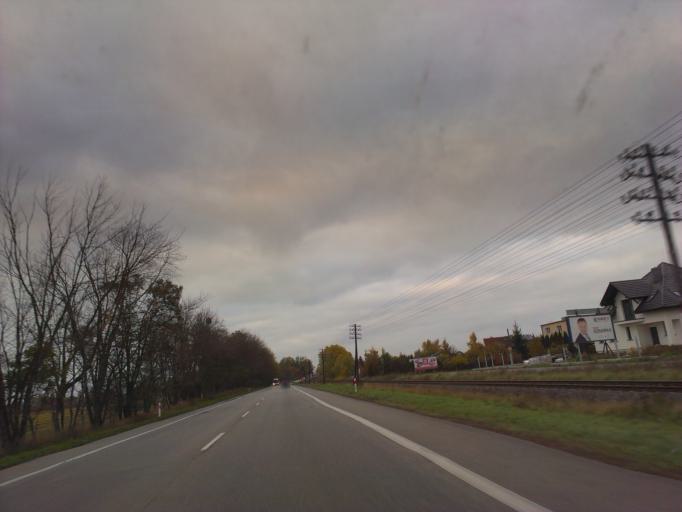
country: PL
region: Kujawsko-Pomorskie
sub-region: Powiat torunski
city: Lysomice
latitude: 53.0772
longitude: 18.6183
